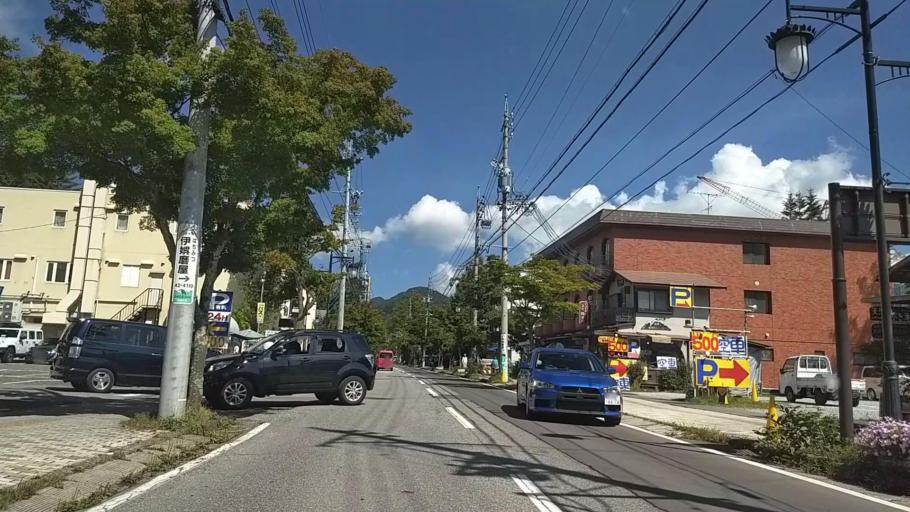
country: JP
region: Nagano
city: Saku
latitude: 36.3504
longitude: 138.6344
